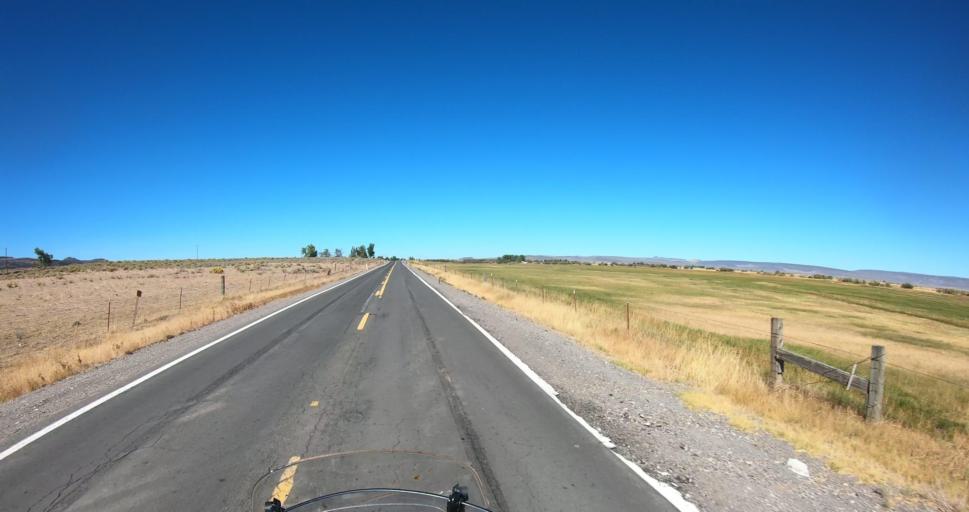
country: US
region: Oregon
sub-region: Lake County
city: Lakeview
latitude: 42.6710
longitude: -120.5260
